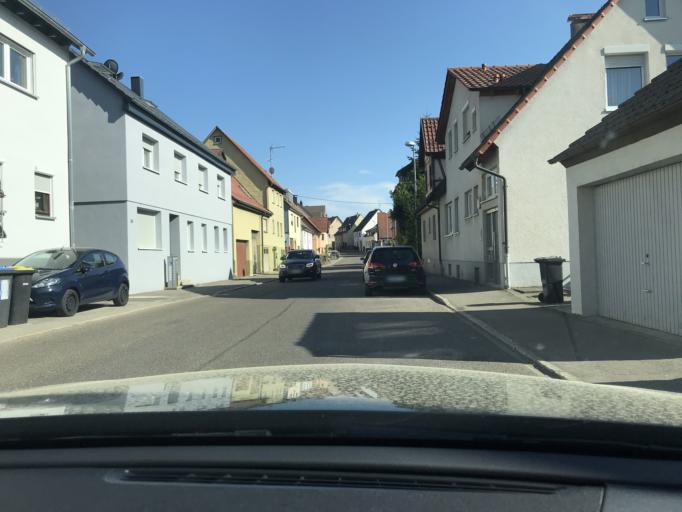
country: DE
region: Baden-Wuerttemberg
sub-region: Regierungsbezirk Stuttgart
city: Weinstadt-Endersbach
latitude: 48.7919
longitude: 9.4013
